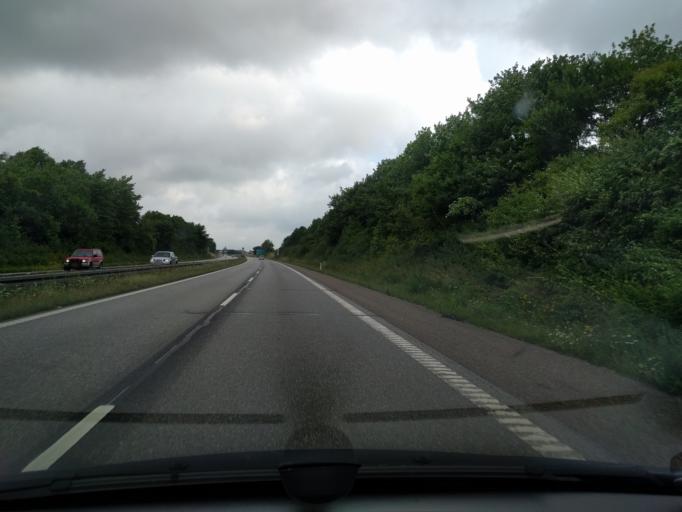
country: DK
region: Zealand
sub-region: Vordingborg Kommune
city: Nyrad
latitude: 54.9828
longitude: 12.0043
